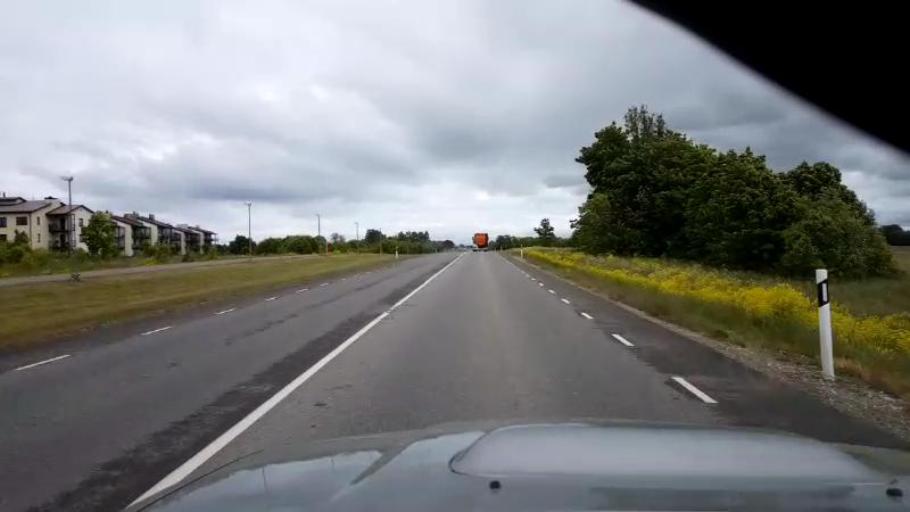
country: EE
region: Harju
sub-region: Harku vald
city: Tabasalu
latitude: 59.4553
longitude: 24.4304
